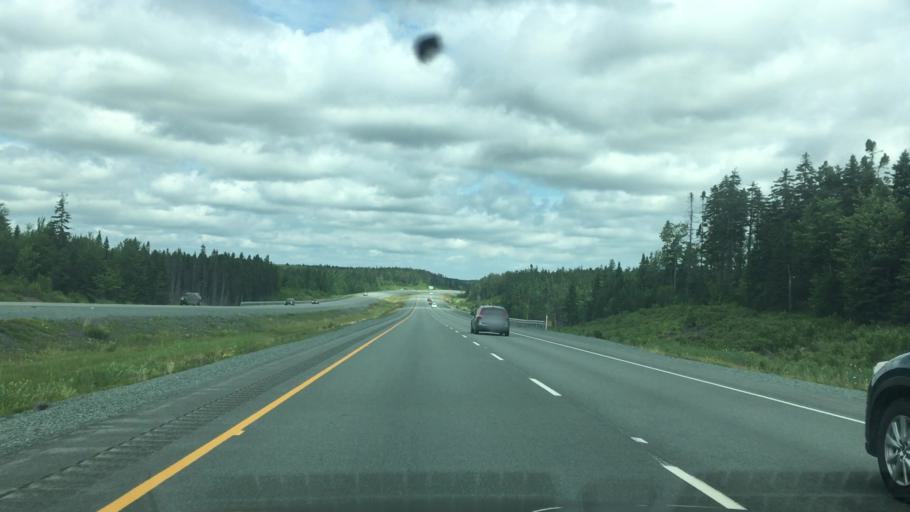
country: CA
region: Nova Scotia
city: Oxford
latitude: 45.6391
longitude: -63.7447
